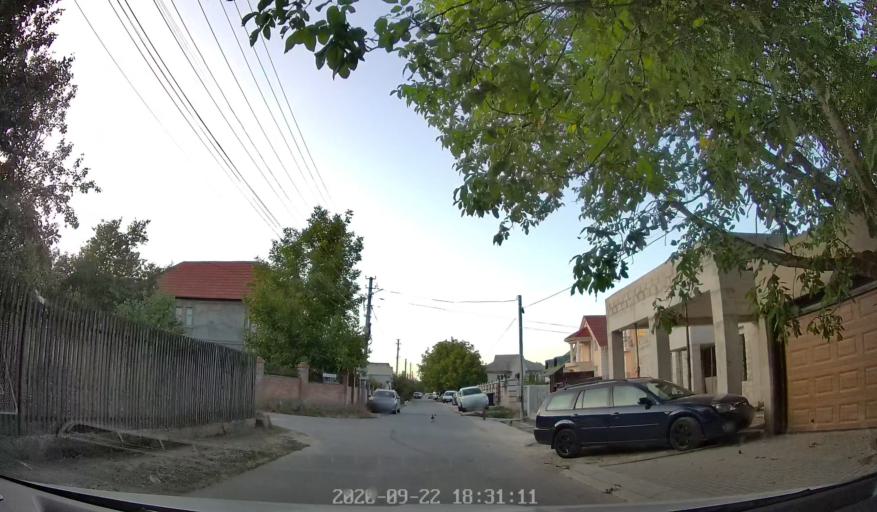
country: MD
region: Laloveni
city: Ialoveni
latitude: 46.9587
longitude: 28.7600
